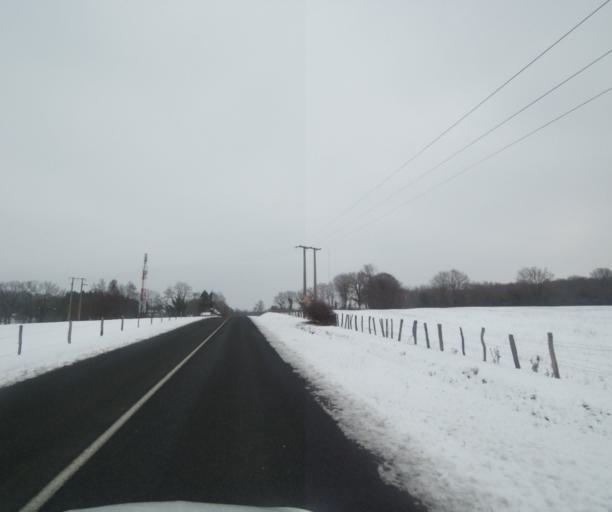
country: FR
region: Champagne-Ardenne
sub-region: Departement de la Haute-Marne
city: Villiers-en-Lieu
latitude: 48.6134
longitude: 4.8881
